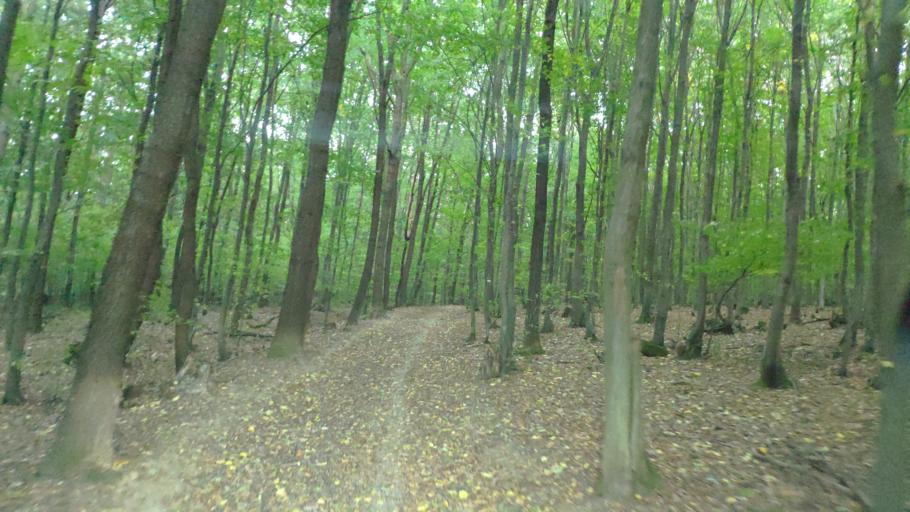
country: SK
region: Kosicky
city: Kosice
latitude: 48.7003
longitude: 21.1935
